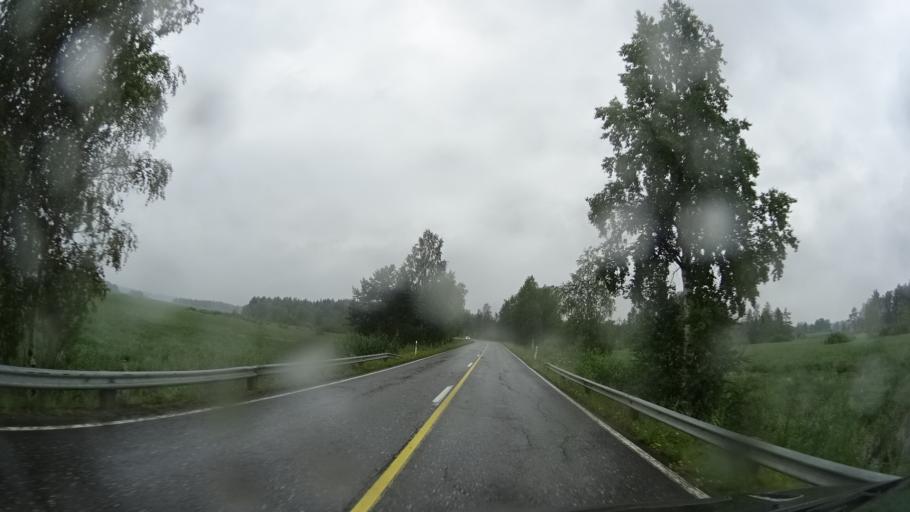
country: FI
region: North Karelia
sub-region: Keski-Karjala
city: Raeaekkylae
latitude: 62.3078
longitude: 29.5357
